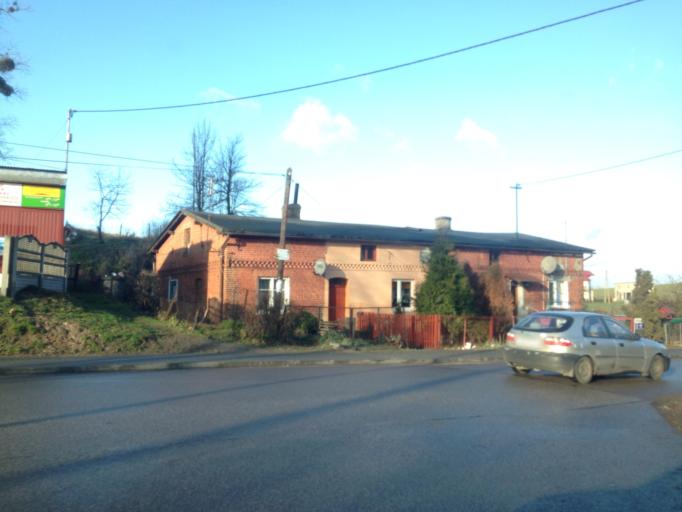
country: PL
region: Kujawsko-Pomorskie
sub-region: Powiat grudziadzki
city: Swiecie nad Osa
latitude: 53.4422
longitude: 19.0978
